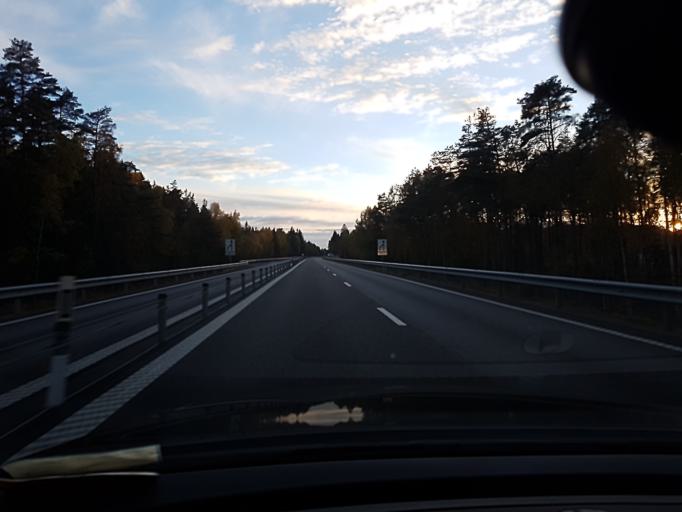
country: SE
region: Kronoberg
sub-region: Ljungby Kommun
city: Ljungby
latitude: 56.7784
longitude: 13.8162
